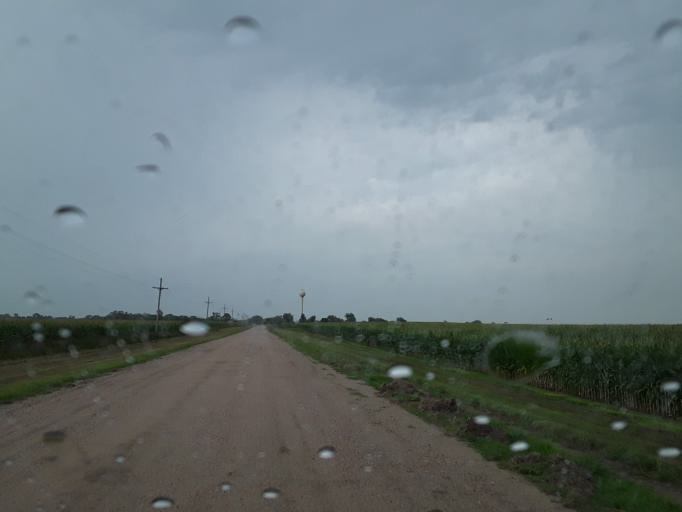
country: US
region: Nebraska
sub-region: Saunders County
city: Yutan
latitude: 41.1775
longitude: -96.4449
